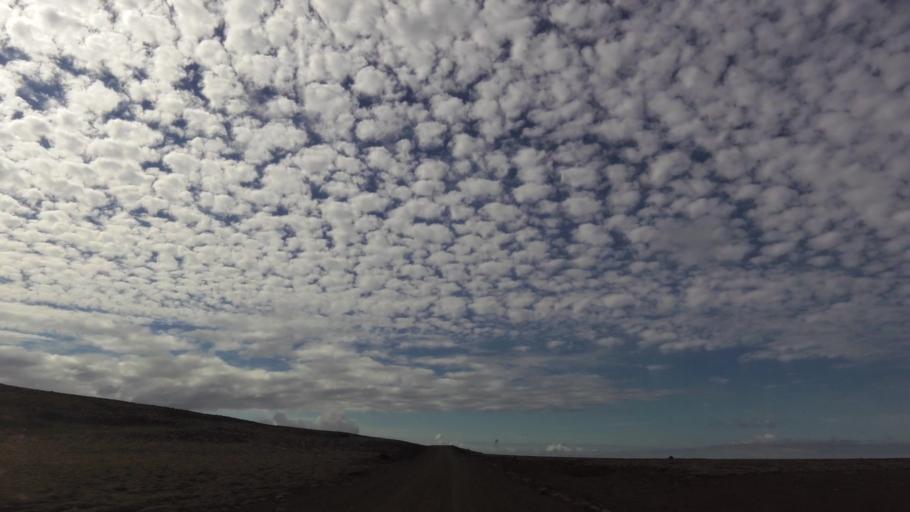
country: IS
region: West
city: Olafsvik
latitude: 65.6191
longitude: -24.2633
